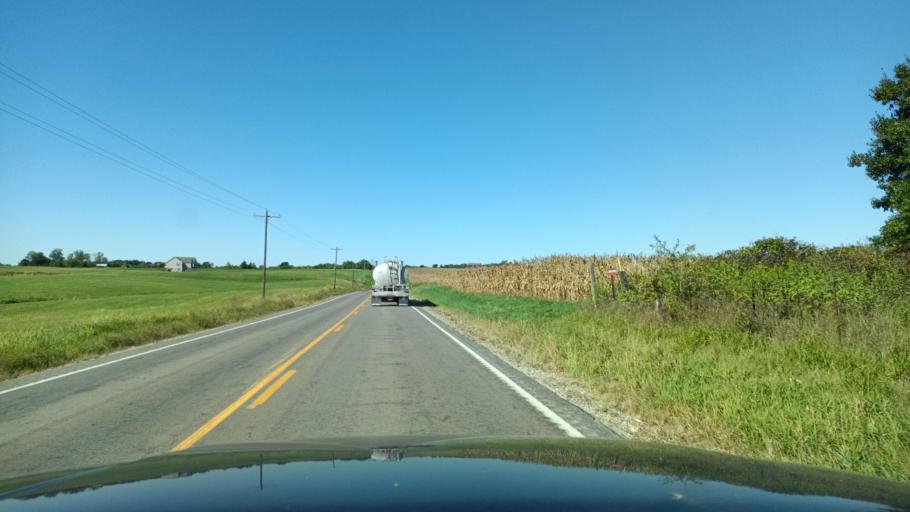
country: US
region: Missouri
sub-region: Scotland County
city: Memphis
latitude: 40.4562
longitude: -92.1255
